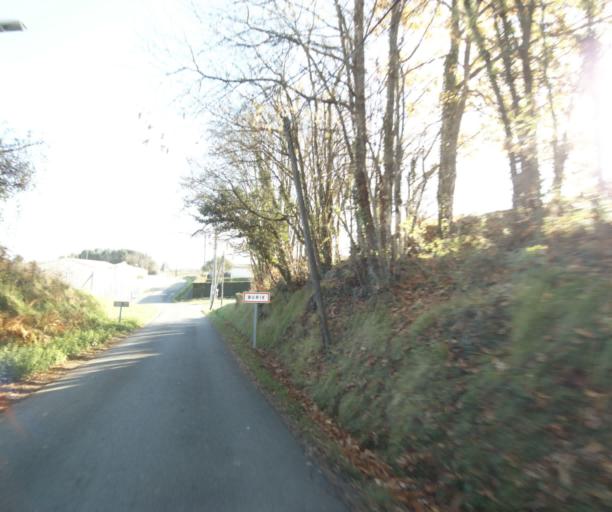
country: FR
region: Poitou-Charentes
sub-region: Departement de la Charente-Maritime
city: Burie
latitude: 45.7735
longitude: -0.4281
